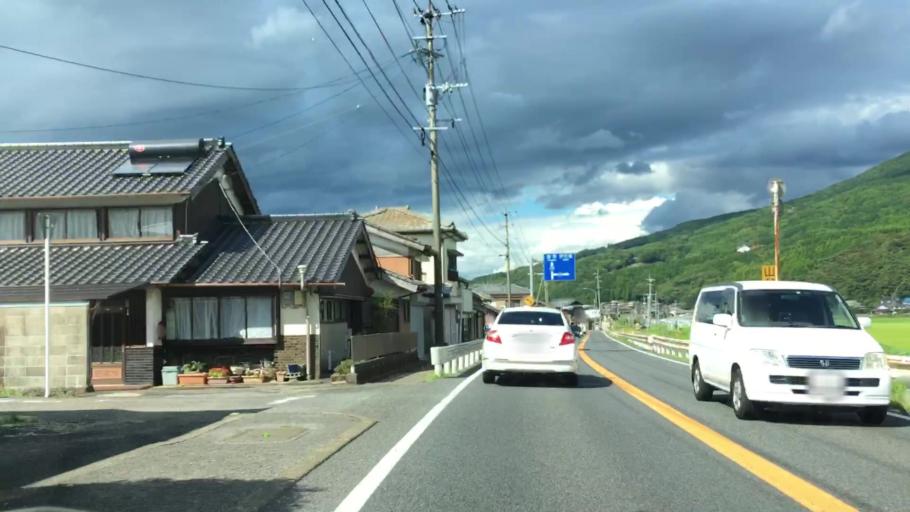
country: JP
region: Saga Prefecture
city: Imaricho-ko
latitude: 33.2272
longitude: 129.8478
